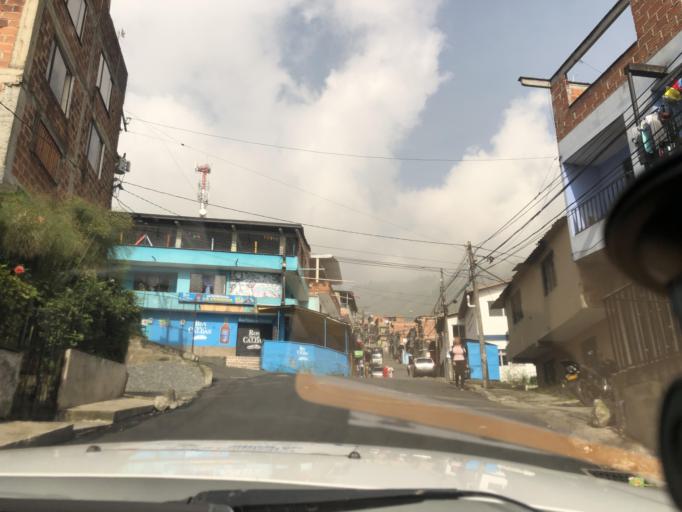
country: CO
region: Antioquia
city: Bello
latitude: 6.3146
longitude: -75.5809
